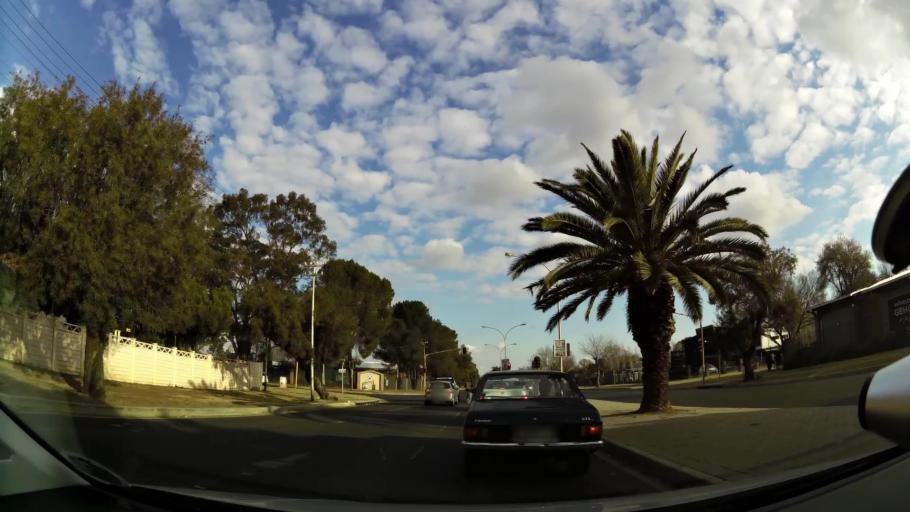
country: ZA
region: Orange Free State
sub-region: Mangaung Metropolitan Municipality
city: Bloemfontein
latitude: -29.1024
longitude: 26.2042
